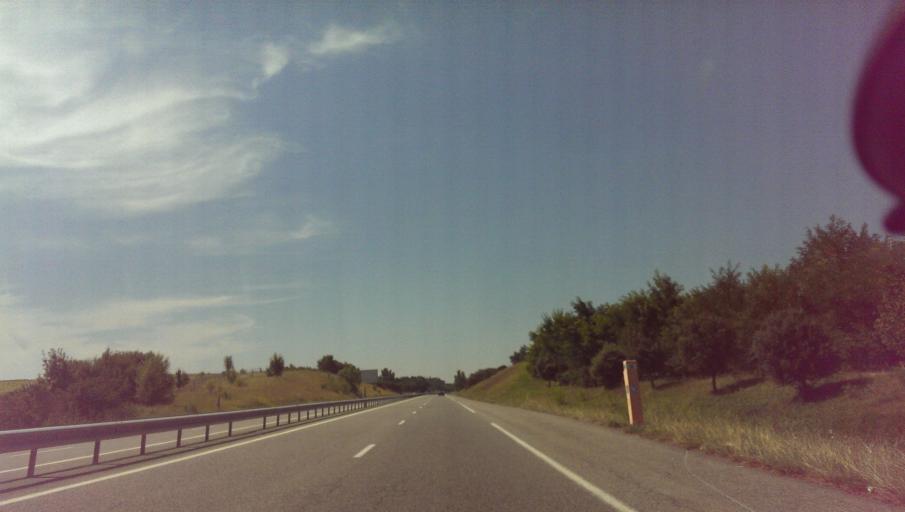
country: FR
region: Midi-Pyrenees
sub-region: Departement de la Haute-Garonne
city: Villenouvelle
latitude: 43.4001
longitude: 1.6404
